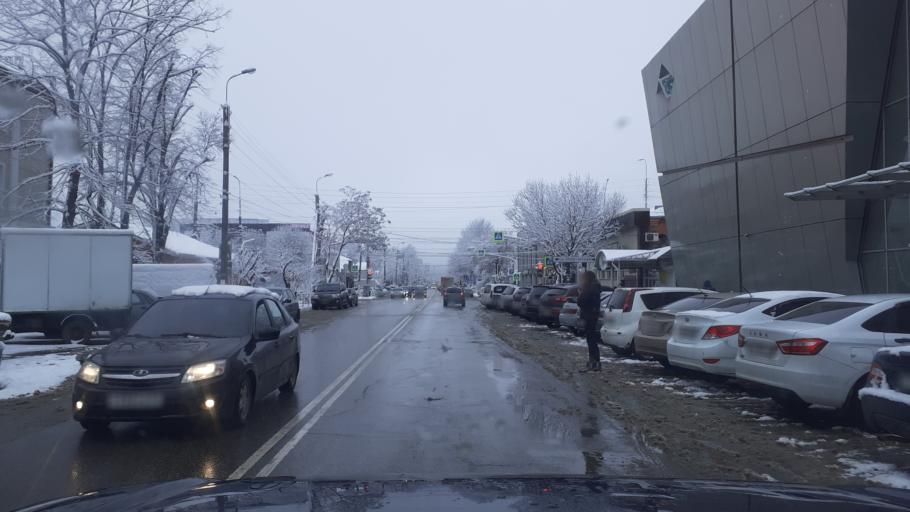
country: RU
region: Adygeya
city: Maykop
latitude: 44.6092
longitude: 40.1120
